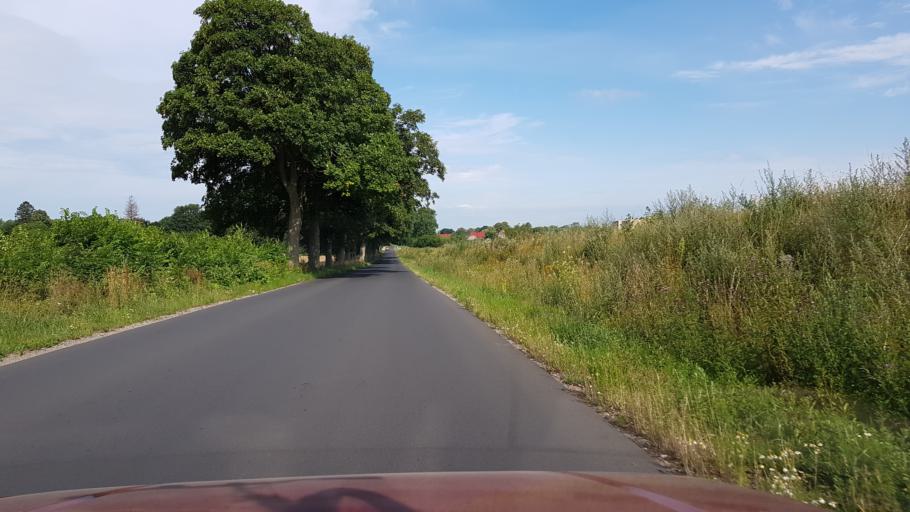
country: PL
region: West Pomeranian Voivodeship
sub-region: Powiat koszalinski
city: Polanow
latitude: 54.1695
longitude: 16.5980
